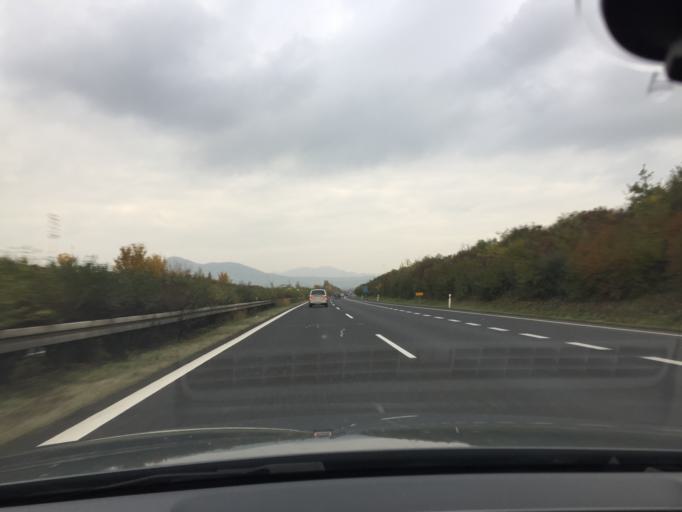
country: CZ
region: Ustecky
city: Lovosice
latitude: 50.4839
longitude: 14.0798
